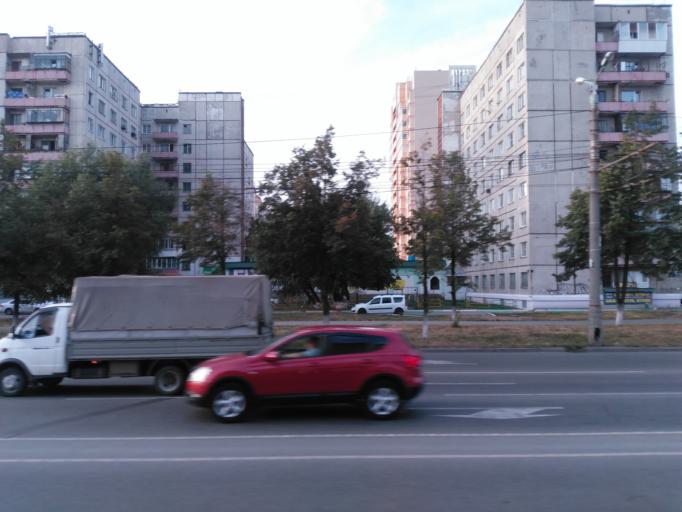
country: RU
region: Chelyabinsk
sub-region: Gorod Chelyabinsk
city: Chelyabinsk
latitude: 55.1918
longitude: 61.3644
